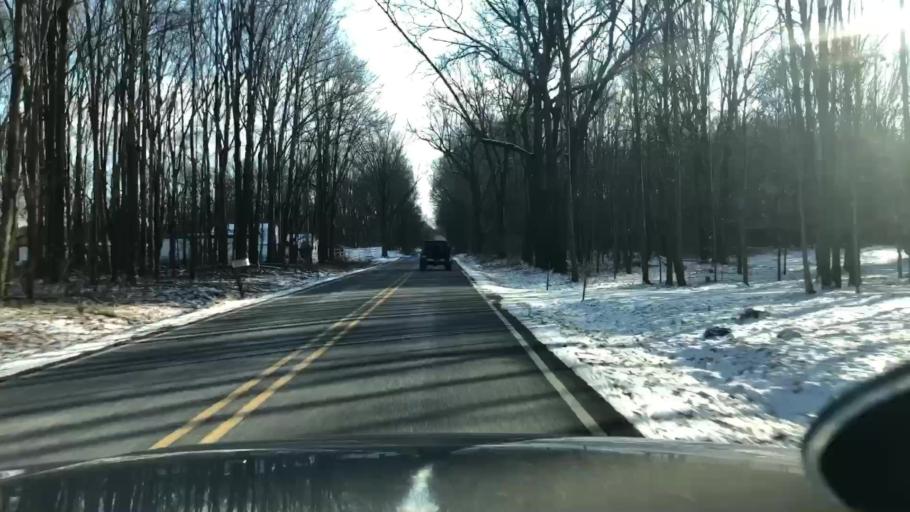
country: US
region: Michigan
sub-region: Jackson County
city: Vandercook Lake
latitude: 42.1119
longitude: -84.4513
